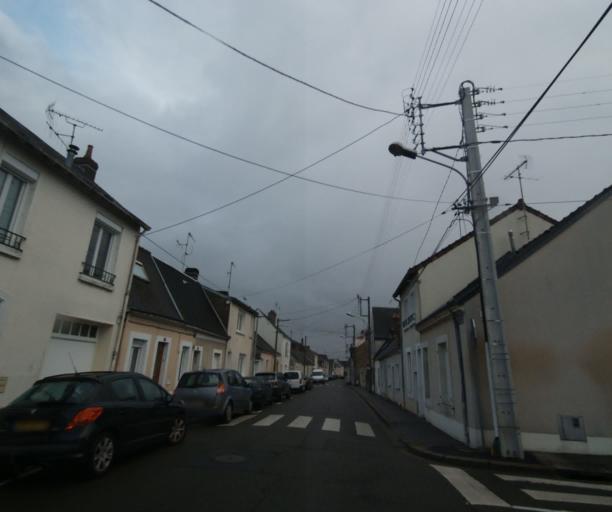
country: FR
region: Pays de la Loire
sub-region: Departement de la Sarthe
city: Coulaines
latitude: 48.0160
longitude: 0.1889
